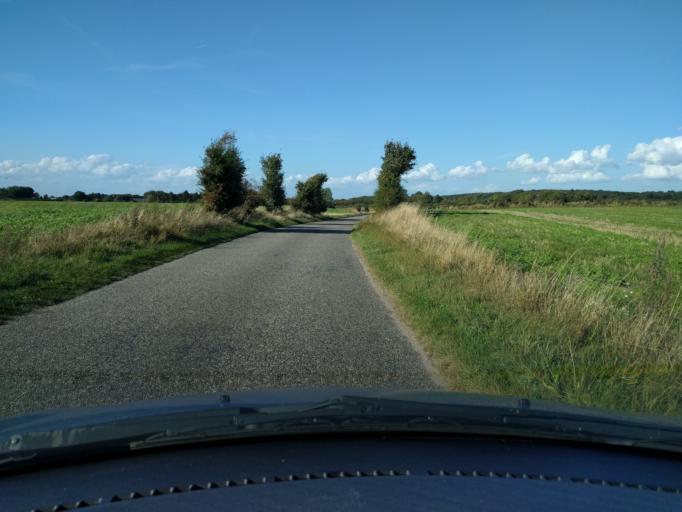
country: DK
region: South Denmark
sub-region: Assens Kommune
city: Harby
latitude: 55.1290
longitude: 10.0321
